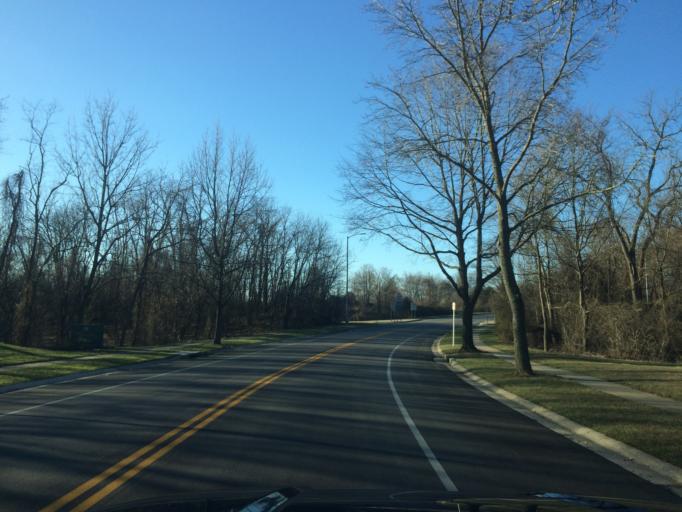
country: US
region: Maryland
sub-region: Howard County
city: Riverside
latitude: 39.1788
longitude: -76.8592
